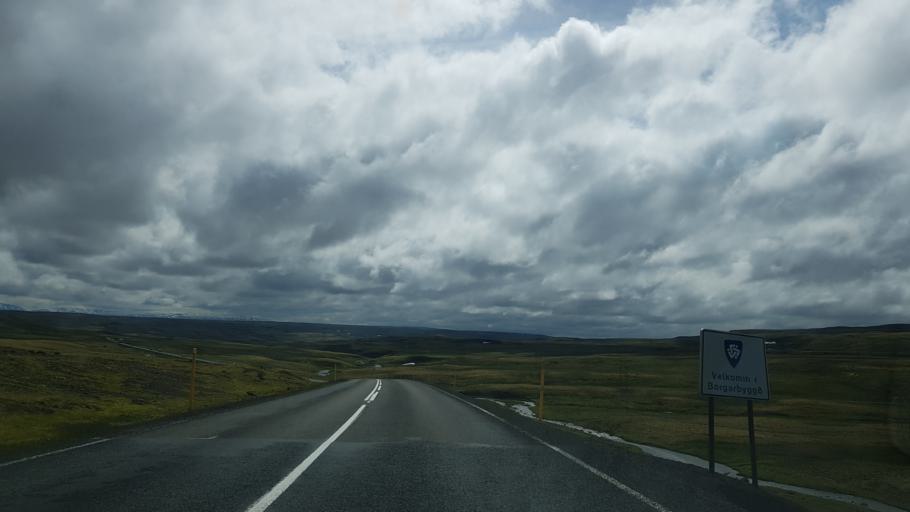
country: IS
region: West
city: Borgarnes
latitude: 64.9726
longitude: -21.0676
